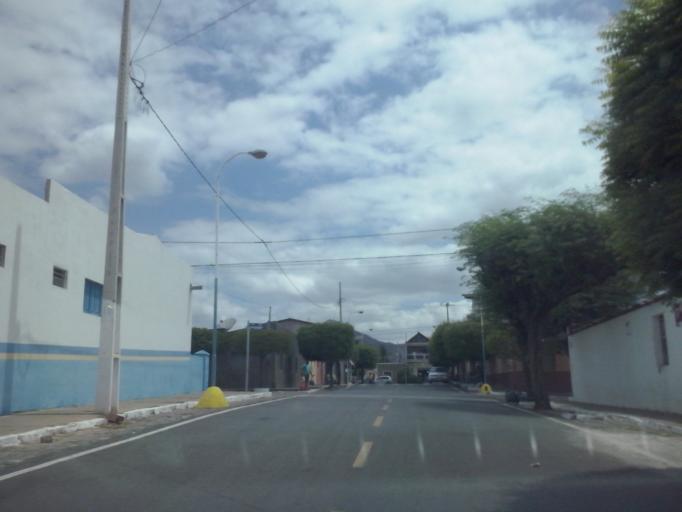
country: BR
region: Paraiba
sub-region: Patos
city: Patos
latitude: -6.9051
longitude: -37.5196
